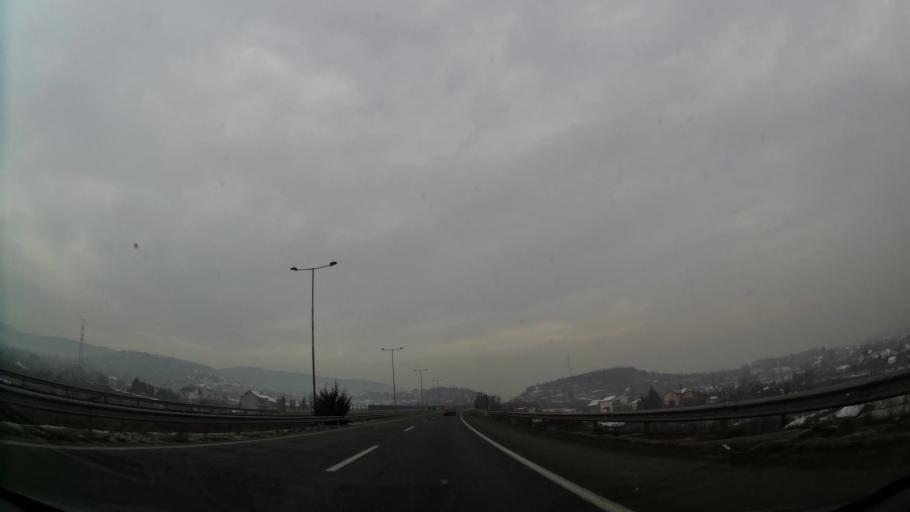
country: MK
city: Kondovo
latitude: 42.0309
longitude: 21.3308
